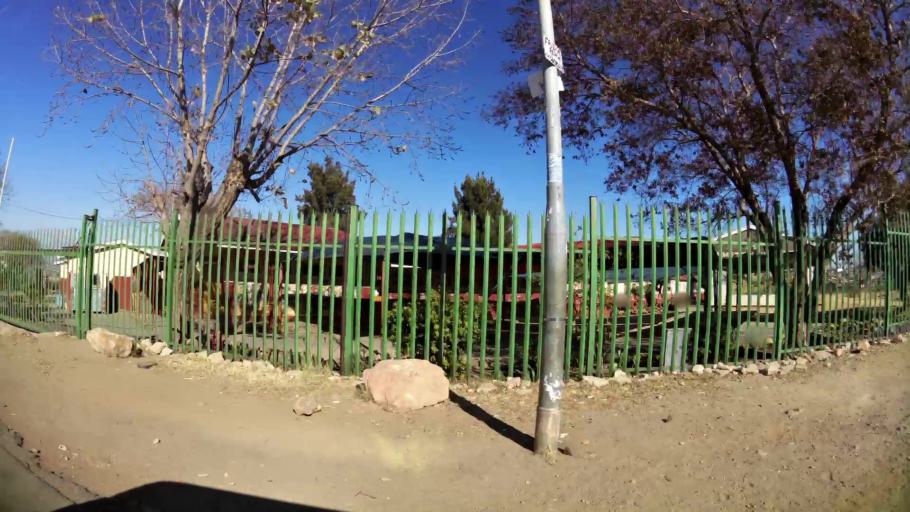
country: ZA
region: Gauteng
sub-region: City of Johannesburg Metropolitan Municipality
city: Soweto
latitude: -26.2222
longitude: 27.9153
